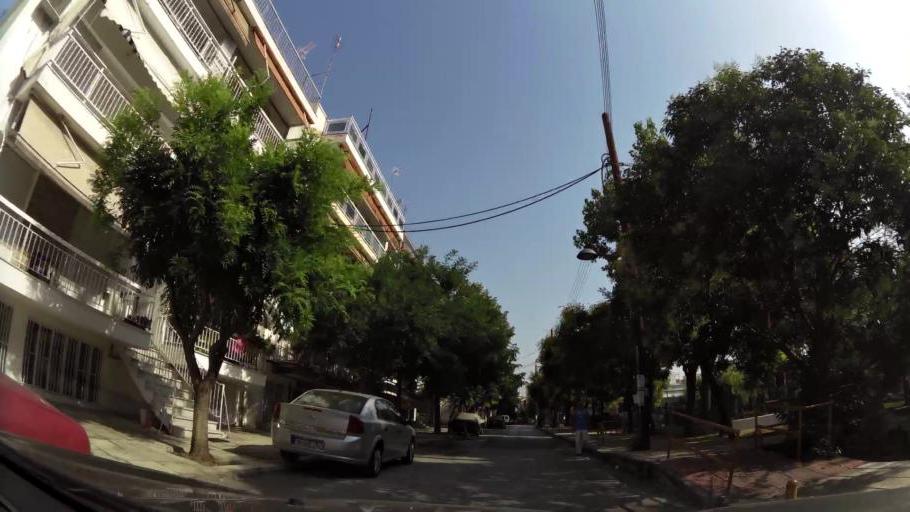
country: GR
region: Central Macedonia
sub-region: Nomos Thessalonikis
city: Stavroupoli
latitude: 40.6682
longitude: 22.9280
